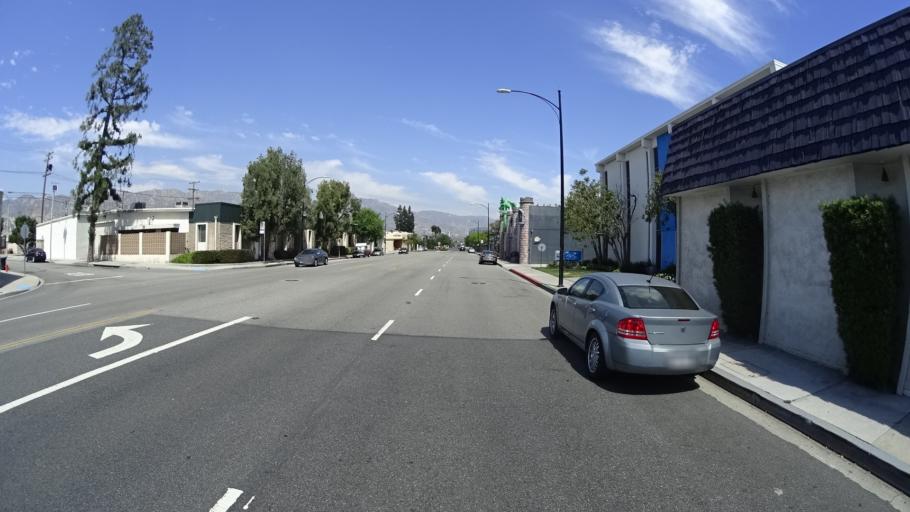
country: US
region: California
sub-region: Los Angeles County
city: Burbank
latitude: 34.1919
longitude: -118.3426
